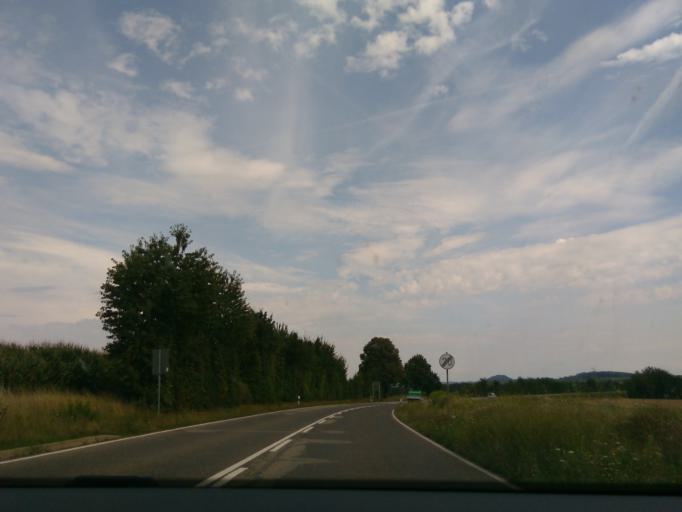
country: DE
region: Baden-Wuerttemberg
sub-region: Regierungsbezirk Stuttgart
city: Neckarwestheim
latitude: 49.0625
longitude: 9.1981
